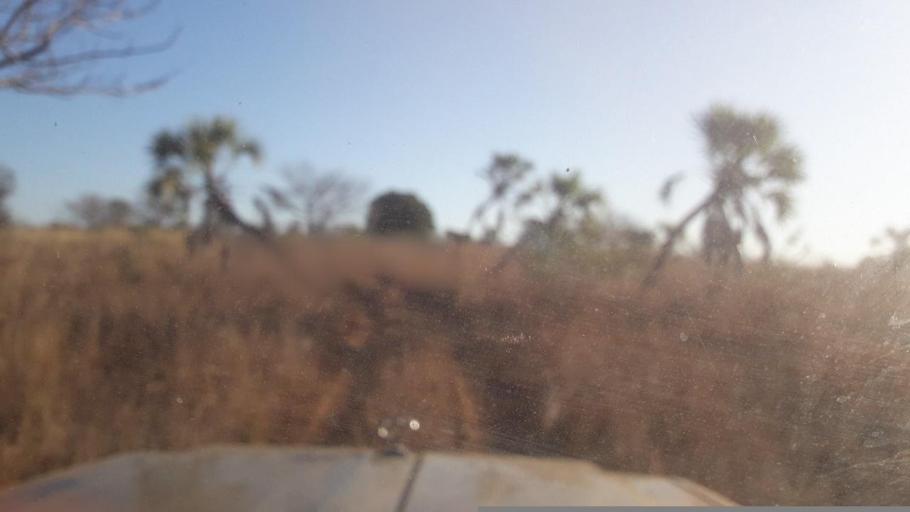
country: MG
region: Boeny
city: Sitampiky
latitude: -16.4978
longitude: 45.6066
